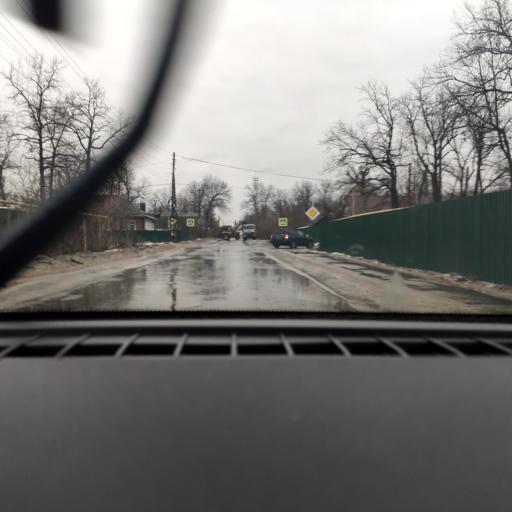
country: RU
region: Voronezj
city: Somovo
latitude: 51.7355
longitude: 39.3573
